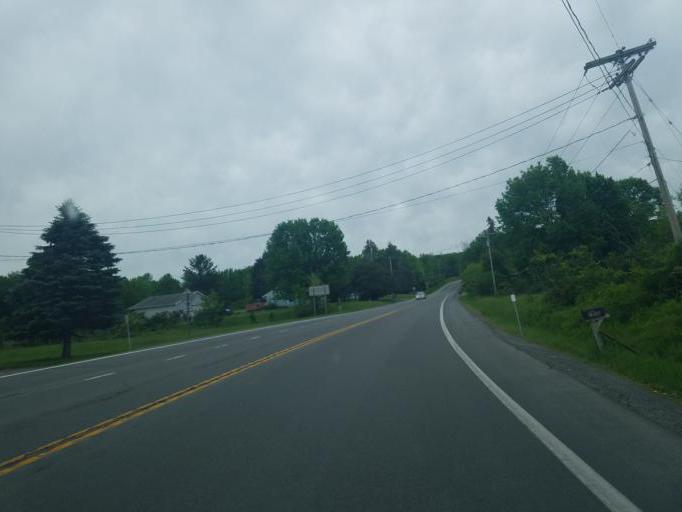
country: US
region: New York
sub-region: Herkimer County
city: Mohawk
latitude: 42.9959
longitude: -75.0082
